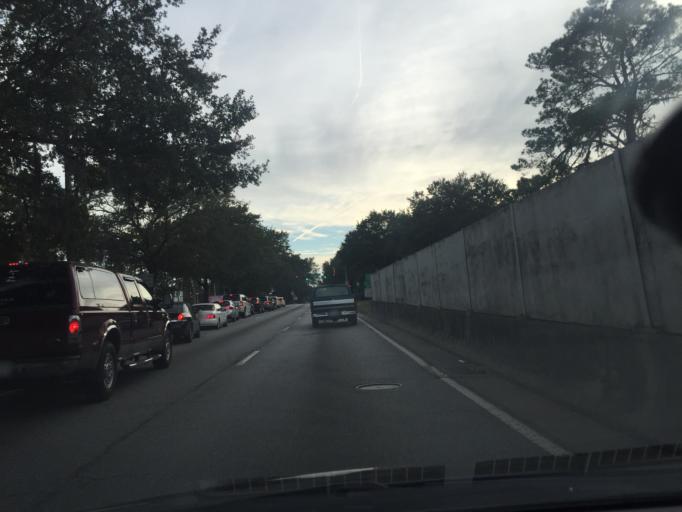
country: US
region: Georgia
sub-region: Chatham County
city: Isle of Hope
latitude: 32.0155
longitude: -81.1155
